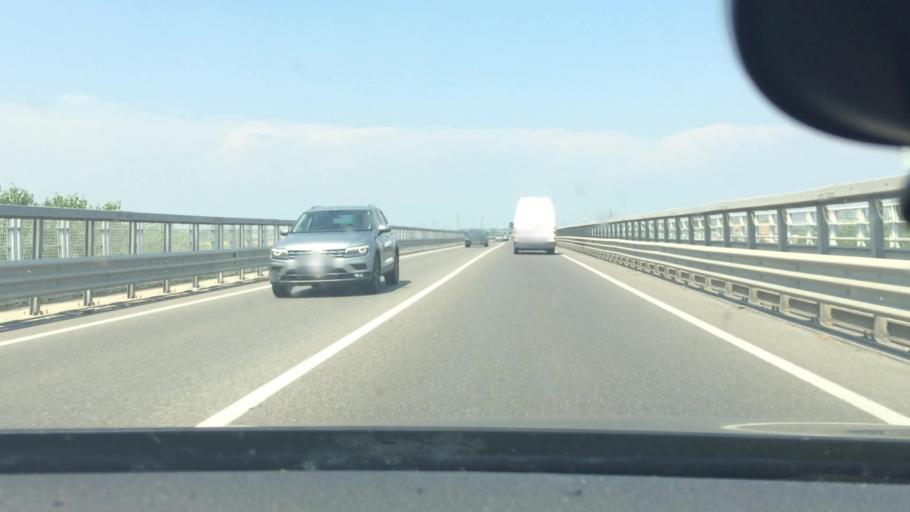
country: IT
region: Lombardy
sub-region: Provincia di Lodi
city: San Rocco al Porto
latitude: 45.0637
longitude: 9.7055
